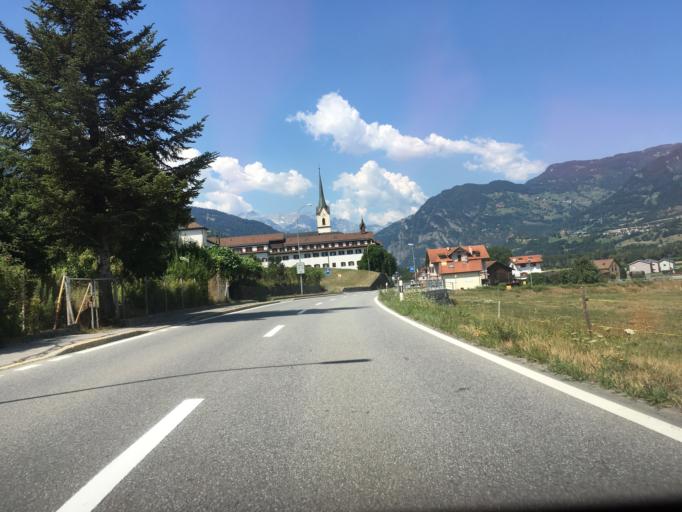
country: CH
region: Grisons
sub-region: Hinterrhein District
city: Cazis
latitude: 46.7193
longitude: 9.4302
